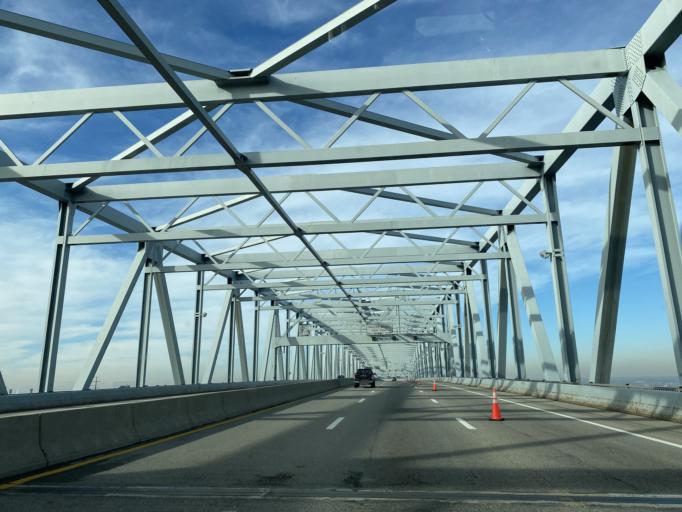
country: US
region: New Jersey
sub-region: Camden County
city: Pennsauken
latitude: 39.9841
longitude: -75.0642
